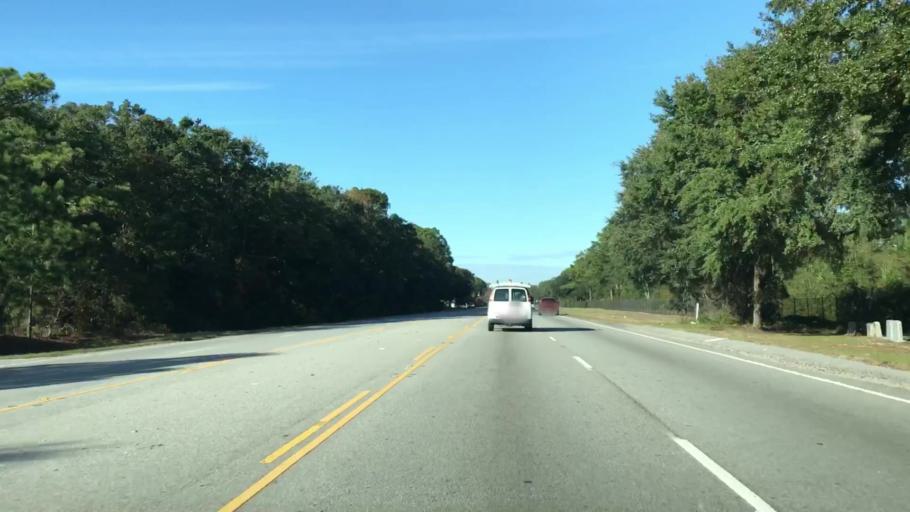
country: US
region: South Carolina
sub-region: Beaufort County
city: Burton
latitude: 32.4692
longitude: -80.7364
